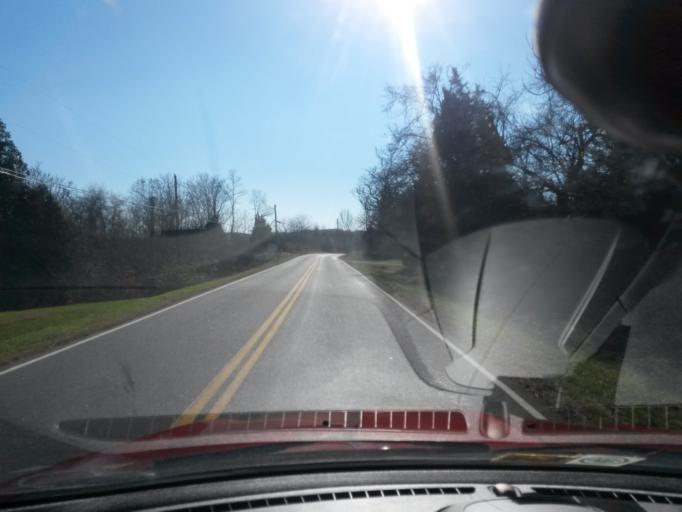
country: US
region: Virginia
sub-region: City of Bedford
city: Bedford
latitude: 37.3996
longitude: -79.5557
